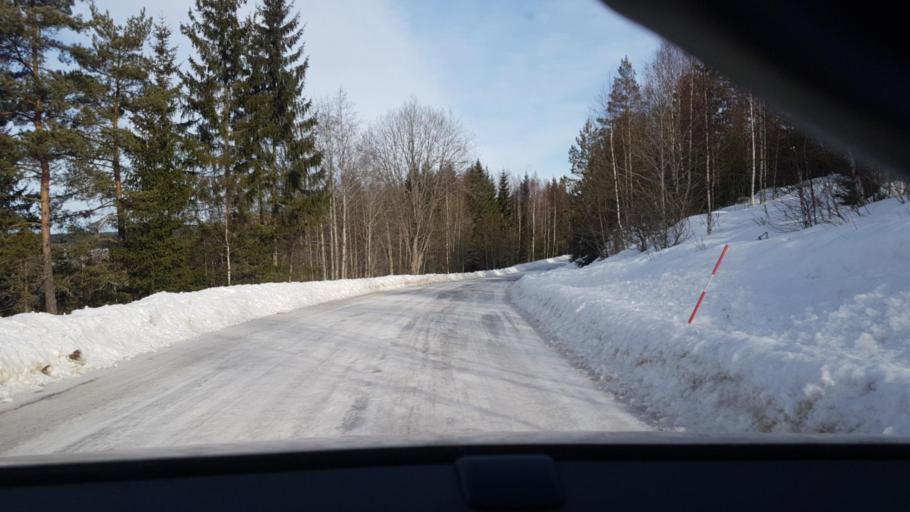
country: NO
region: Ostfold
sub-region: Romskog
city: Romskog
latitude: 59.8359
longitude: 11.9828
